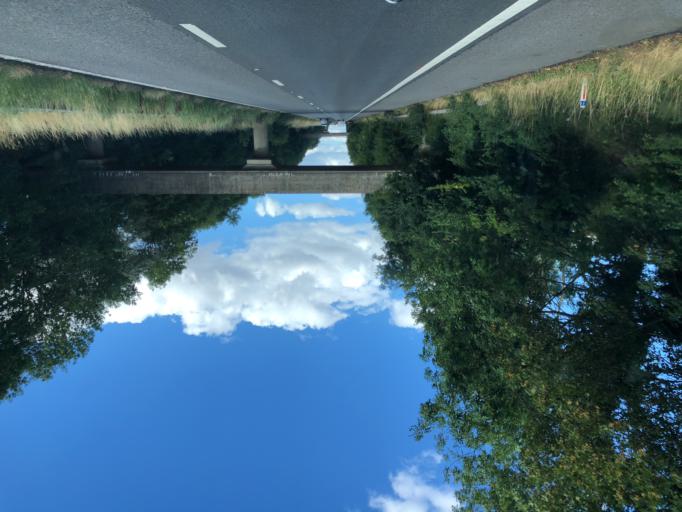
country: GB
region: England
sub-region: Northamptonshire
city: Daventry
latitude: 52.3317
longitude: -1.1807
